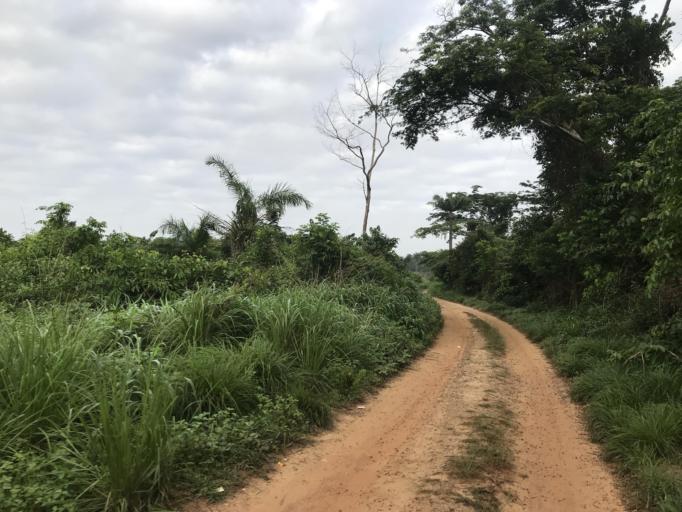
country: SL
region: Eastern Province
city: Pendembu
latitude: 8.0892
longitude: -10.6954
